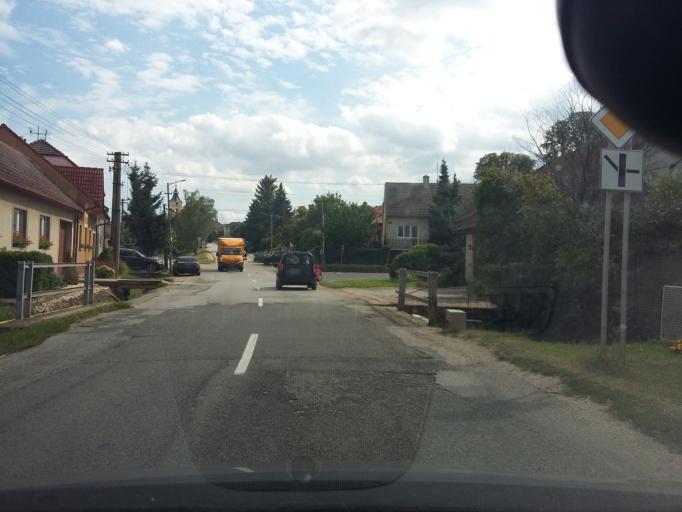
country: SK
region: Trnavsky
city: Gbely
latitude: 48.7243
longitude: 17.1609
